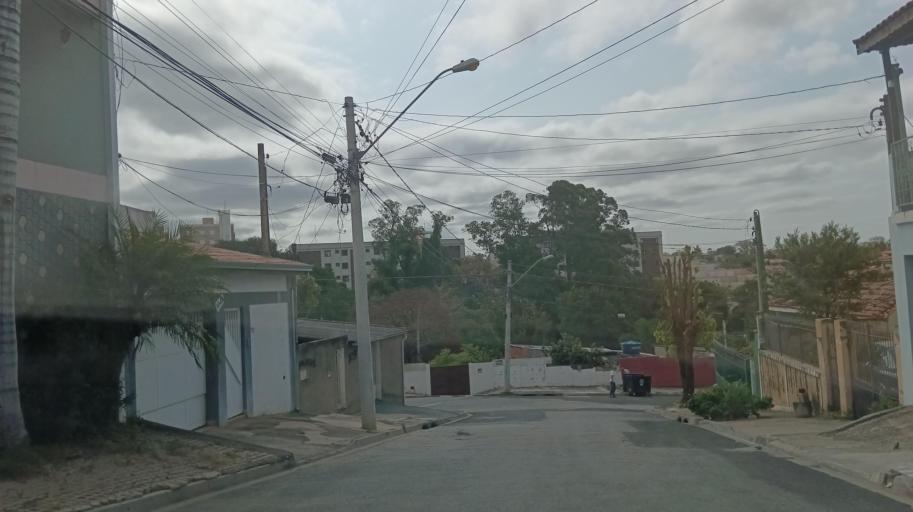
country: BR
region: Sao Paulo
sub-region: Sorocaba
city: Sorocaba
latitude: -23.4727
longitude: -47.4672
